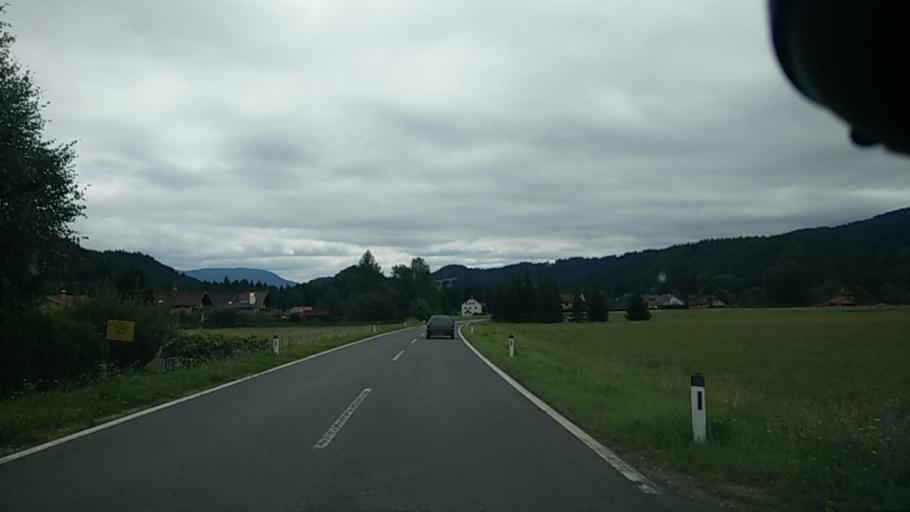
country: AT
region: Carinthia
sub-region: Politischer Bezirk Villach Land
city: Rosegg
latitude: 46.5538
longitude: 13.9866
